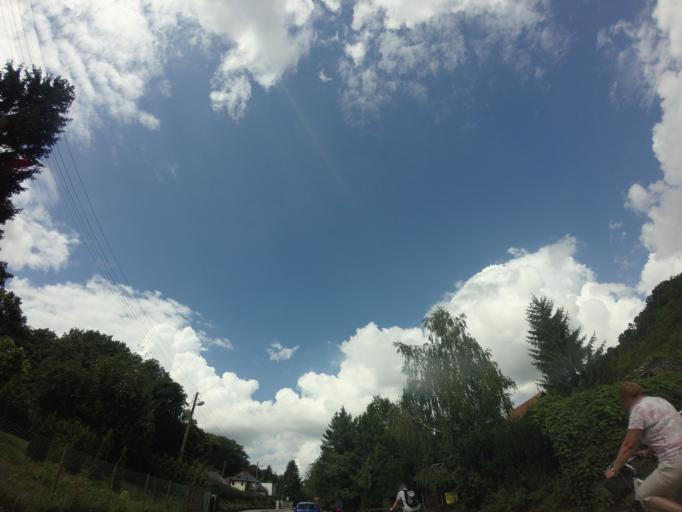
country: PL
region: Lublin Voivodeship
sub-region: Powiat pulawski
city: Kazimierz Dolny
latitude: 51.3196
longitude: 21.9532
